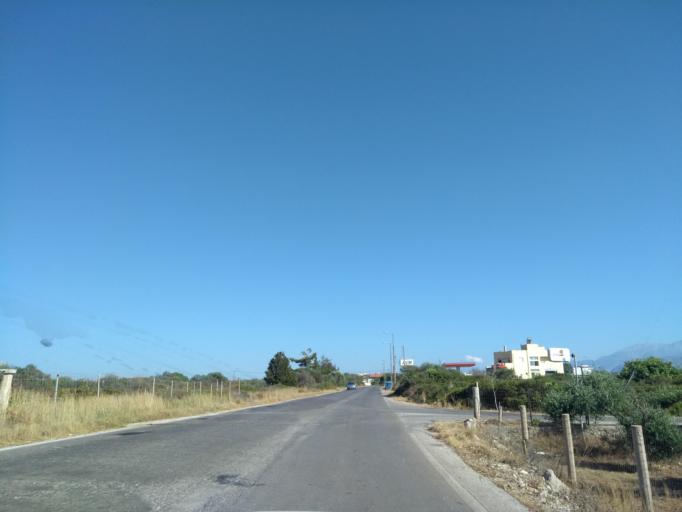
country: GR
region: Crete
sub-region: Nomos Chanias
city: Pithari
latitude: 35.5820
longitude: 24.0921
